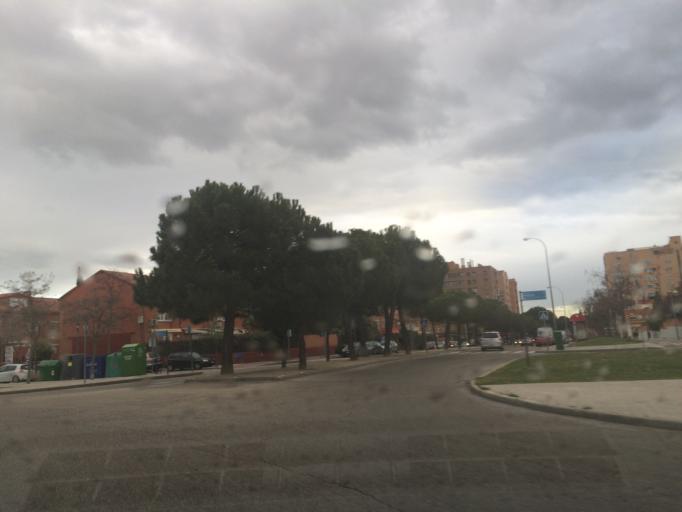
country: ES
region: Madrid
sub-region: Provincia de Madrid
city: Tres Cantos
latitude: 40.6026
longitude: -3.7086
